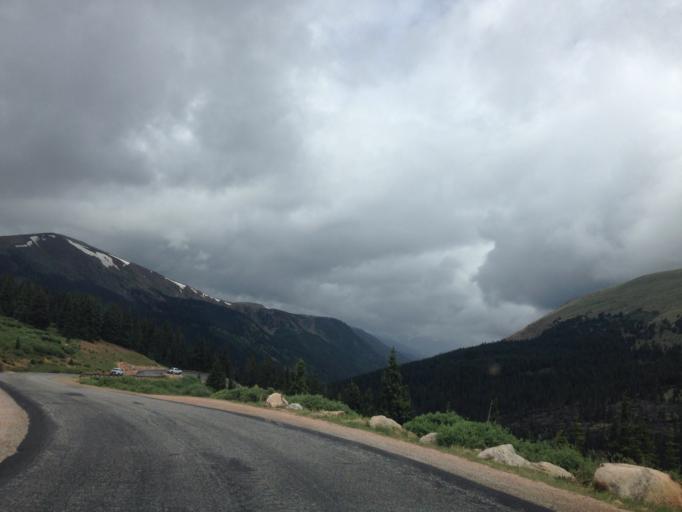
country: US
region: Colorado
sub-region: Clear Creek County
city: Georgetown
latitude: 39.5983
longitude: -105.7093
